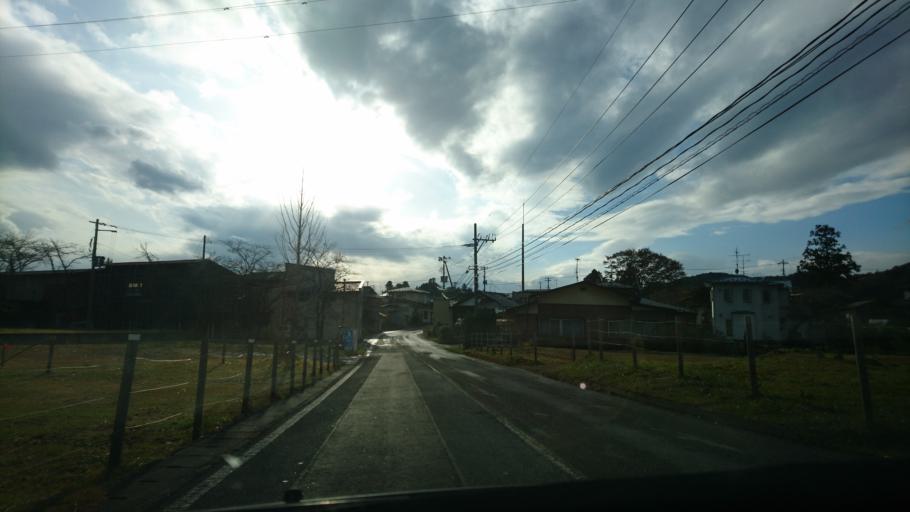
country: JP
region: Iwate
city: Ichinoseki
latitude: 38.9925
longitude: 141.1184
